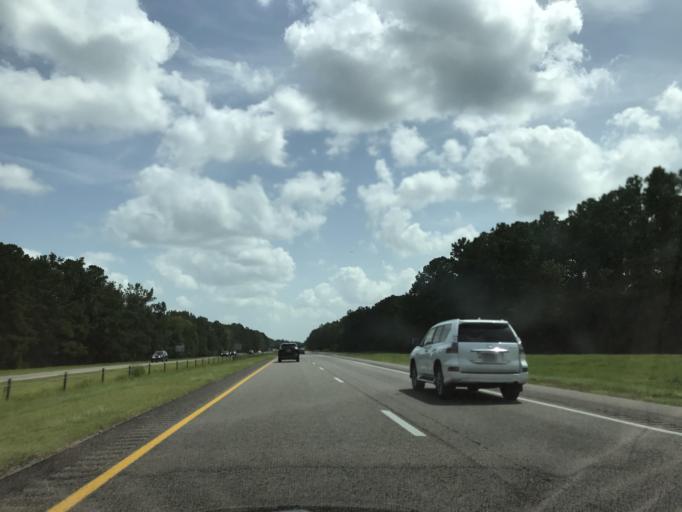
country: US
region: North Carolina
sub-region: Pender County
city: Burgaw
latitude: 34.5745
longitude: -77.9015
